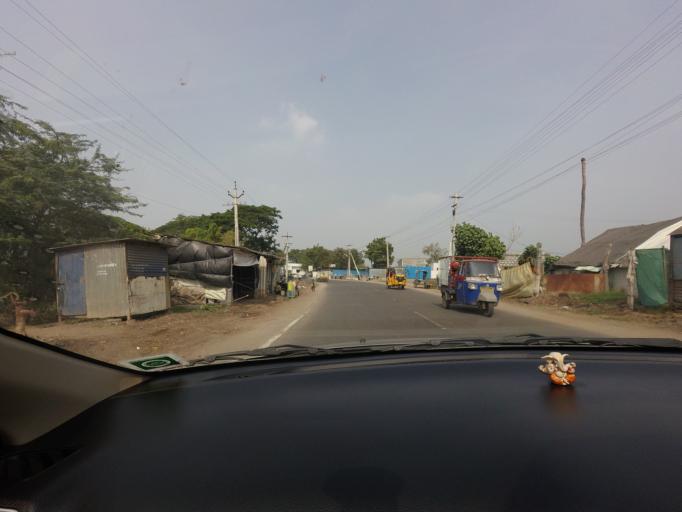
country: IN
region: Andhra Pradesh
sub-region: Krishna
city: Kankipadu
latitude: 16.4380
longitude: 80.7691
